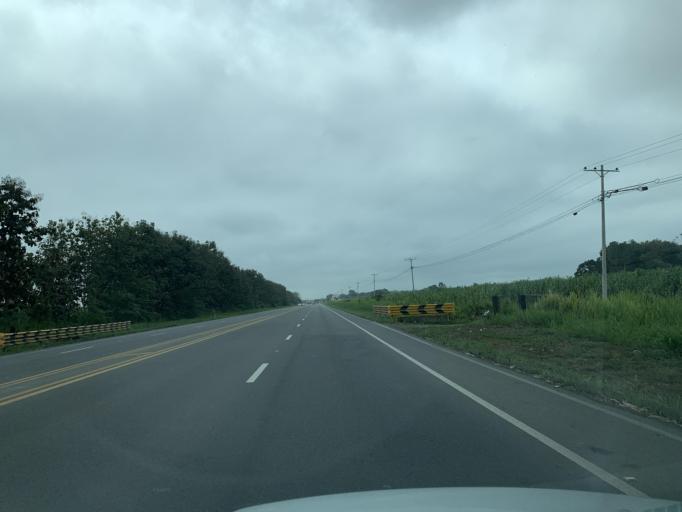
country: EC
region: Guayas
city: Coronel Marcelino Mariduena
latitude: -2.3109
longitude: -79.4765
